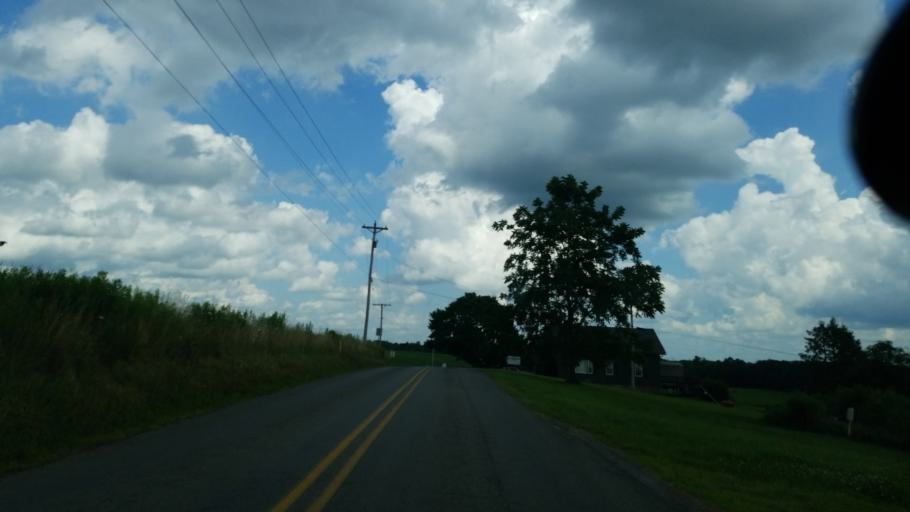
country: US
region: Pennsylvania
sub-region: Jefferson County
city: Brookville
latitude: 41.2307
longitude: -79.0904
